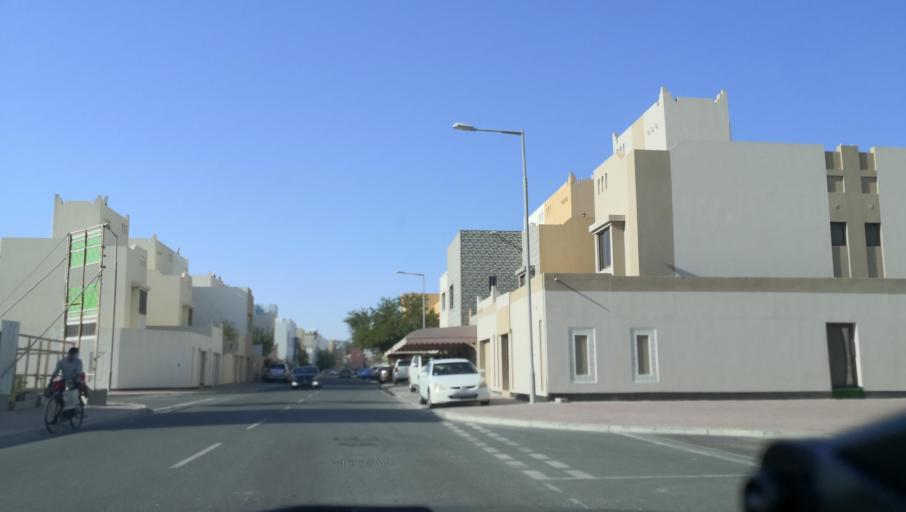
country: BH
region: Muharraq
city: Al Hadd
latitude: 26.2495
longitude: 50.6338
